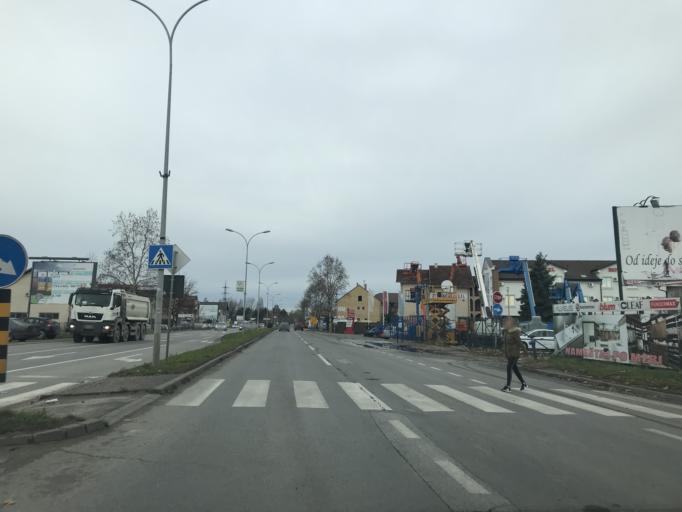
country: RS
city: Veternik
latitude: 45.2437
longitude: 19.7823
